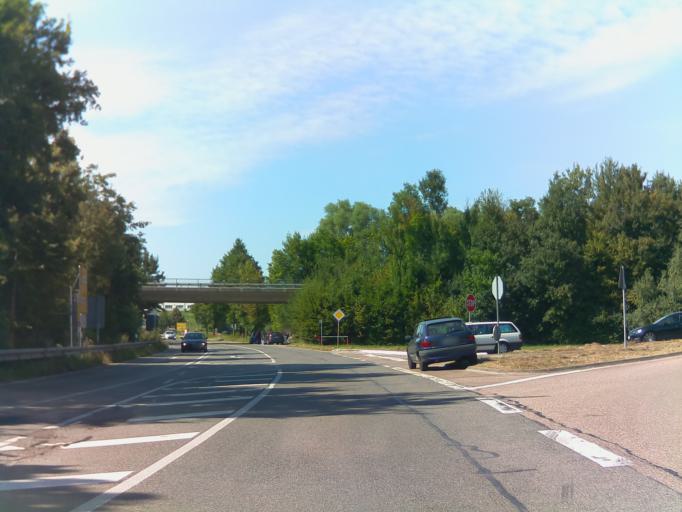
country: DE
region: Baden-Wuerttemberg
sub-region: Karlsruhe Region
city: Oberderdingen
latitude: 49.0791
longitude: 8.7836
